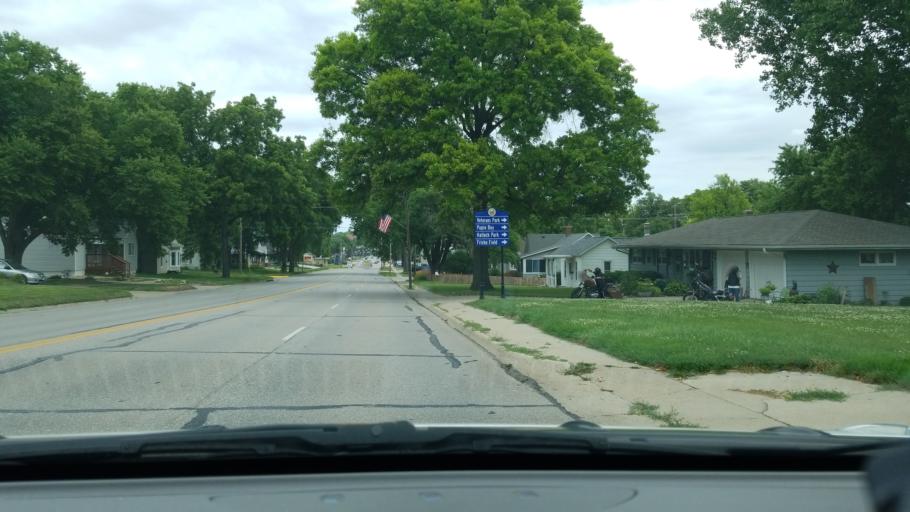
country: US
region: Nebraska
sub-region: Sarpy County
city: Papillion
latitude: 41.1498
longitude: -96.0429
